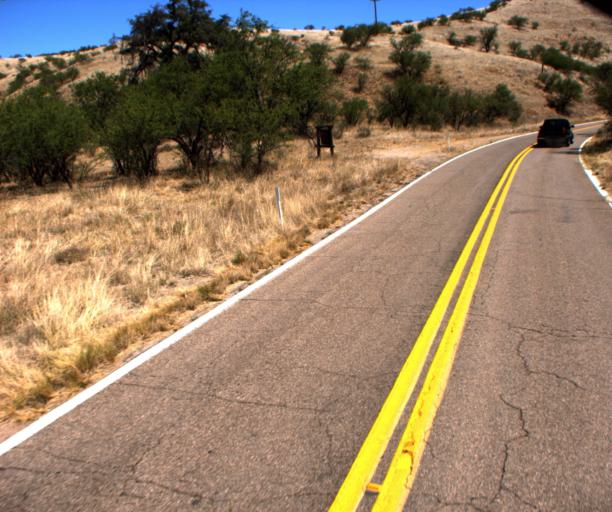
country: US
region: Arizona
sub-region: Santa Cruz County
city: Rio Rico
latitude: 31.3934
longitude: -111.0448
